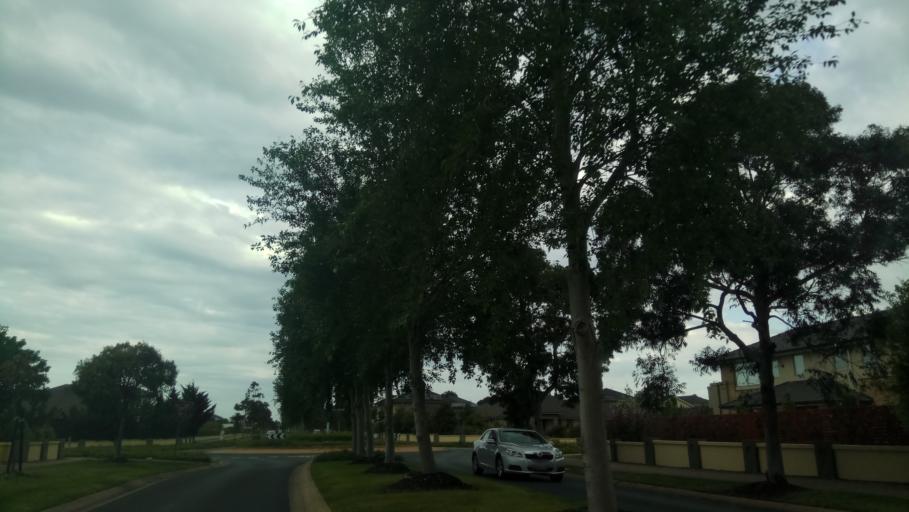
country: AU
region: Victoria
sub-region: Hobsons Bay
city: Altona Meadows
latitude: -37.8887
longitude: 144.7710
